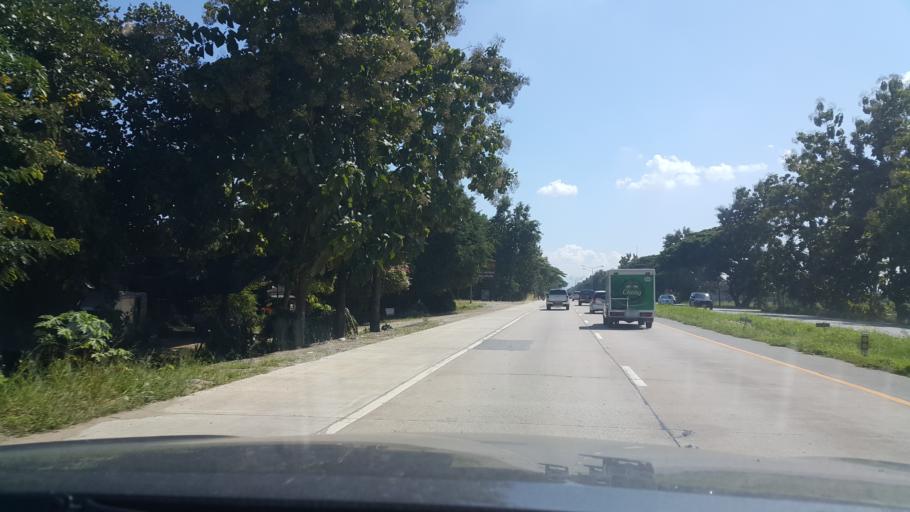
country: TH
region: Chiang Mai
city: Saraphi
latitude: 18.6642
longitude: 99.0520
